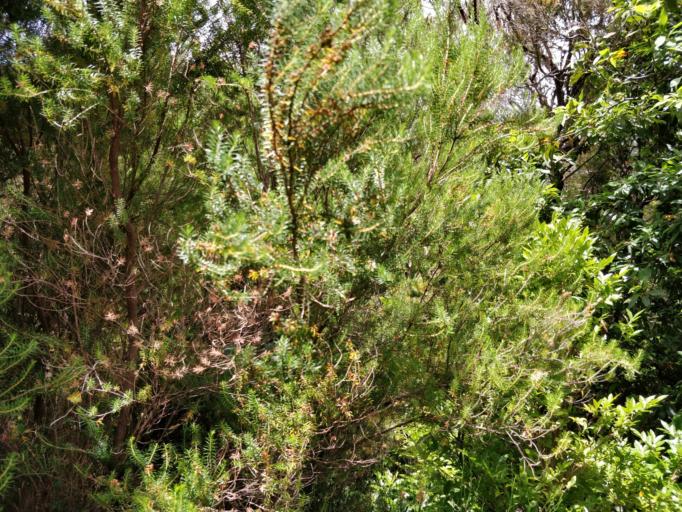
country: PT
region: Madeira
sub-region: Calheta
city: Arco da Calheta
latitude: 32.7623
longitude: -17.1276
